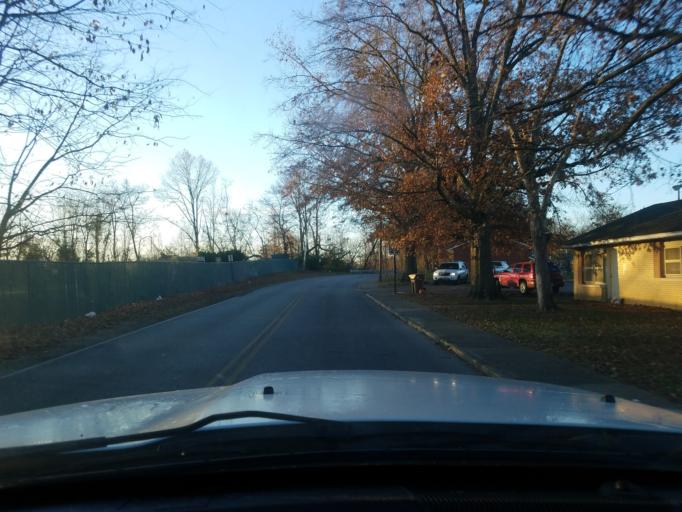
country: US
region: Indiana
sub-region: Floyd County
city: New Albany
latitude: 38.2976
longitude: -85.8235
